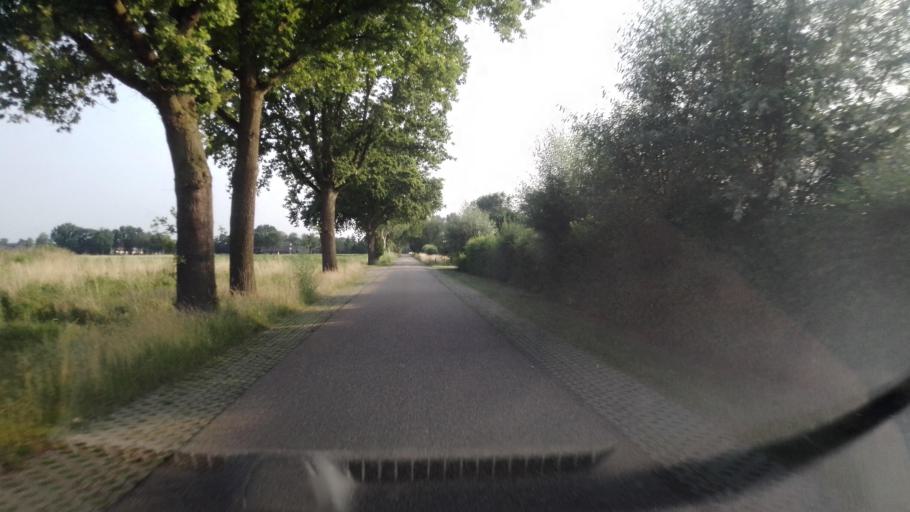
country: NL
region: Limburg
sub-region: Gemeente Peel en Maas
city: Maasbree
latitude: 51.4082
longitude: 6.0591
